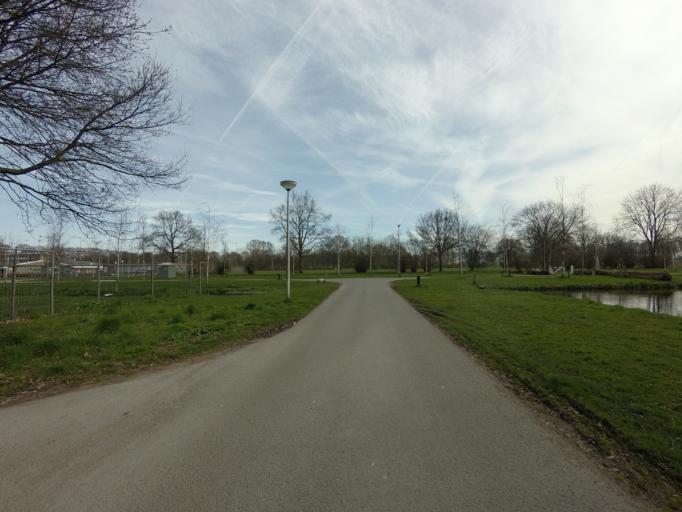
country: NL
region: South Holland
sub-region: Gemeente Alphen aan den Rijn
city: Alphen aan den Rijn
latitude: 52.1267
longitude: 4.6753
